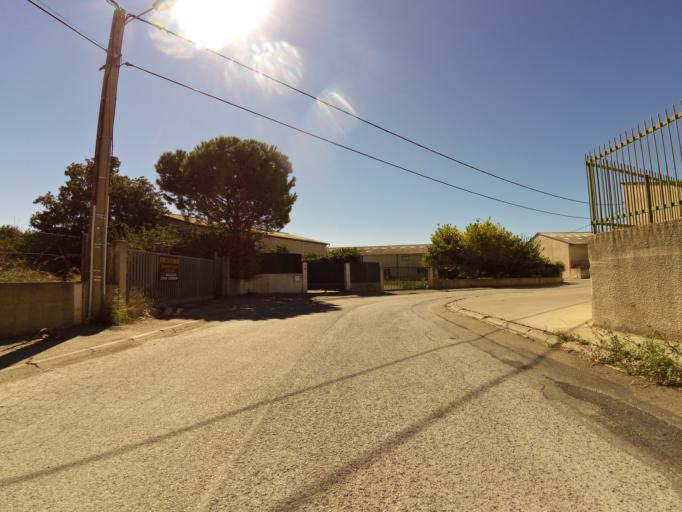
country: FR
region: Languedoc-Roussillon
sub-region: Departement du Gard
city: Codognan
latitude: 43.7270
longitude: 4.2150
